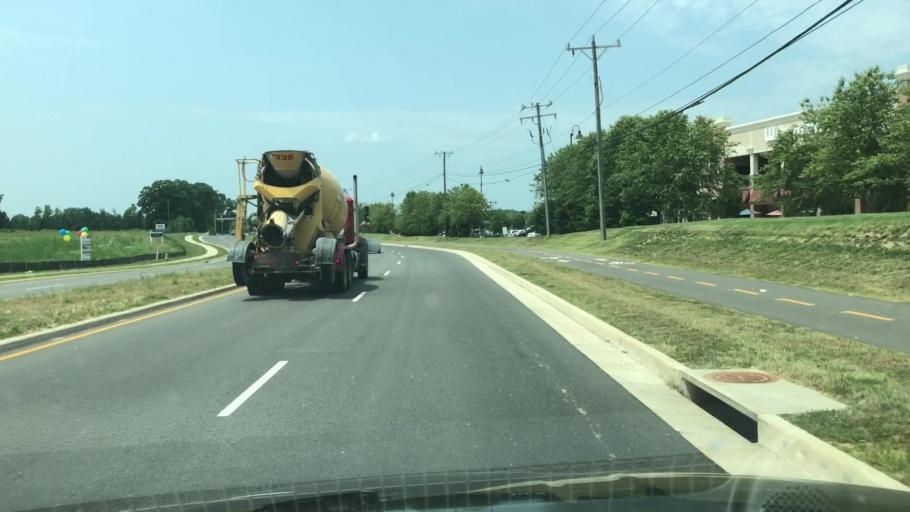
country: US
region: Virginia
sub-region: Stafford County
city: Falmouth
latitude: 38.3124
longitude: -77.5071
